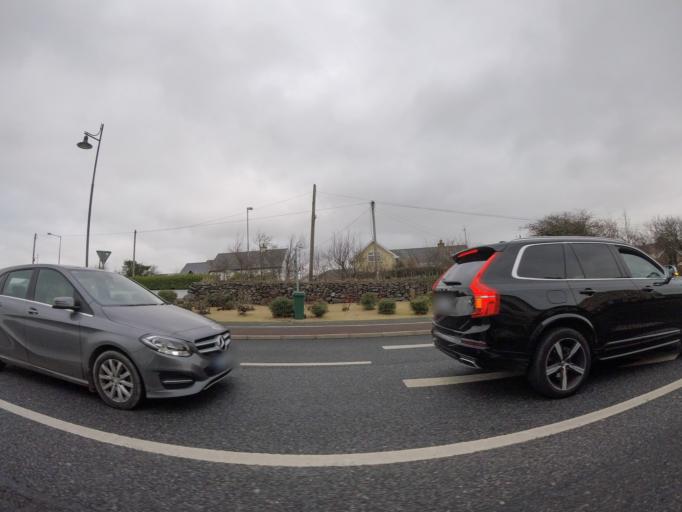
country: IE
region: Munster
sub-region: Waterford
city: Tra Mhor
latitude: 52.1648
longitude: -7.1614
